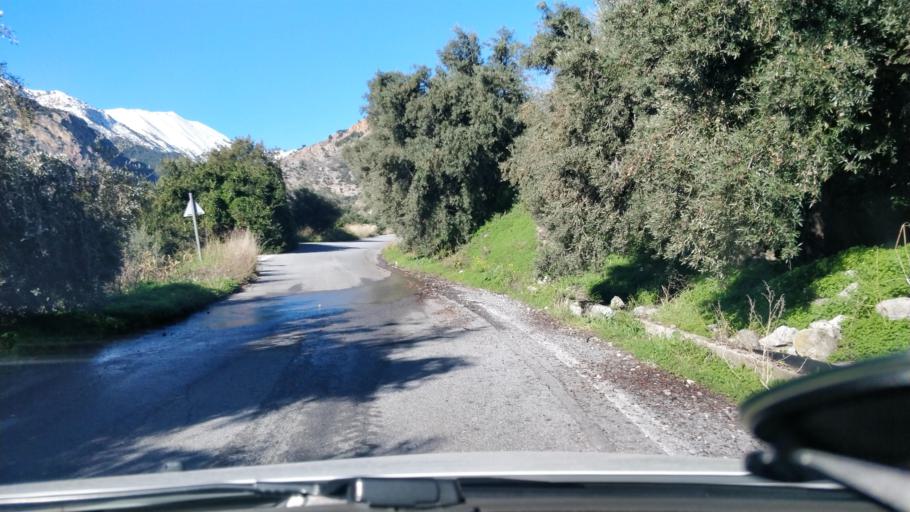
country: GR
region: Crete
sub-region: Nomos Lasithiou
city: Kritsa
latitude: 35.0771
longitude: 25.5843
